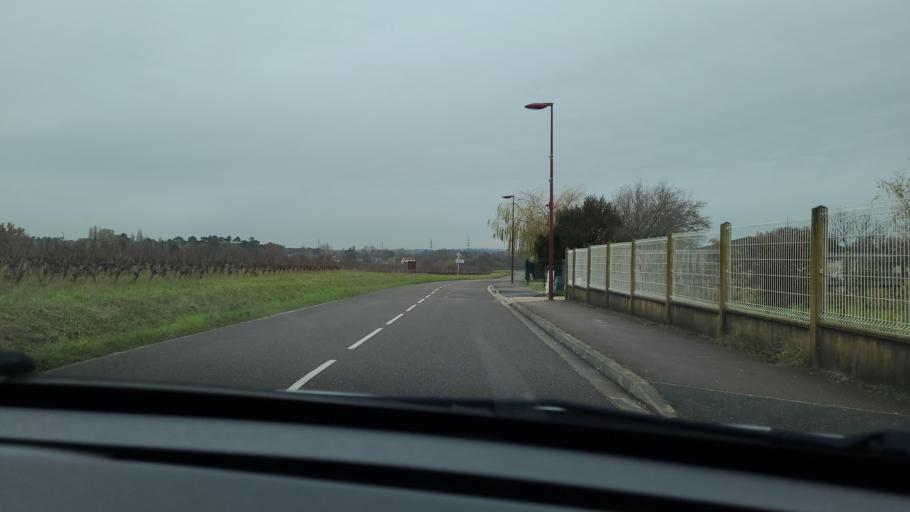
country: FR
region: Aquitaine
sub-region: Departement de la Gironde
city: Pugnac
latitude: 45.0842
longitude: -0.4898
